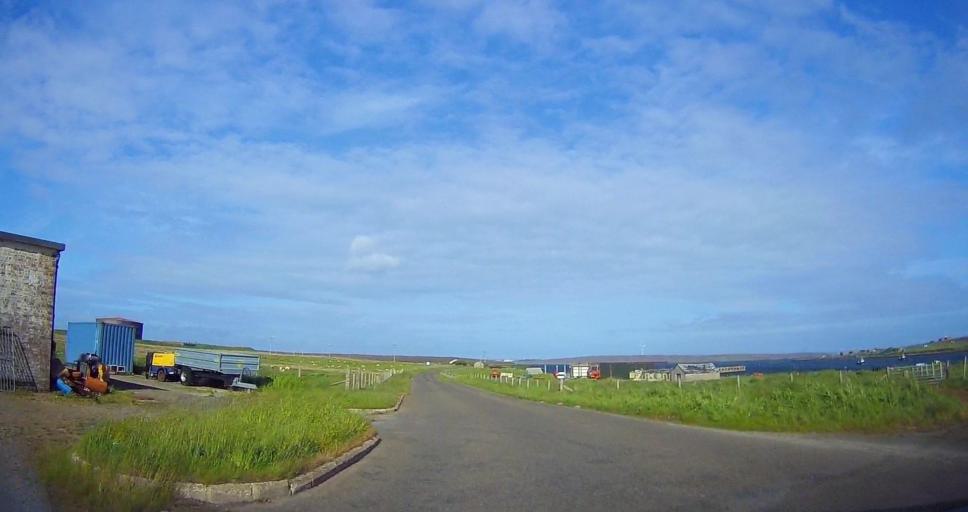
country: GB
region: Scotland
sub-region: Orkney Islands
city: Stromness
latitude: 58.8311
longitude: -3.2039
